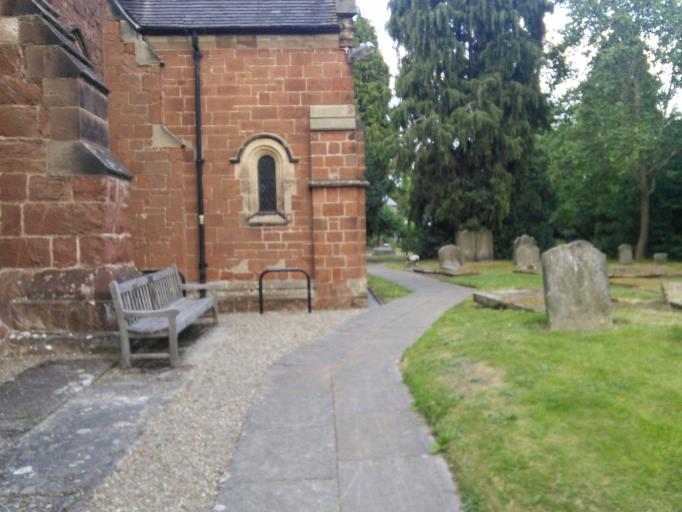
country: GB
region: England
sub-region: Shropshire
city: Shrewsbury
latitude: 52.7019
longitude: -2.7308
